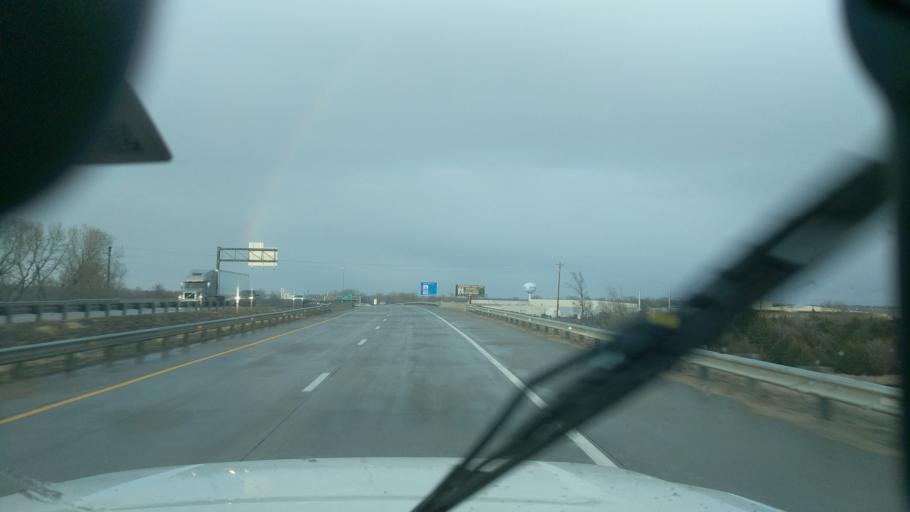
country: US
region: Kansas
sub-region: Harvey County
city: Newton
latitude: 38.0342
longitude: -97.3247
